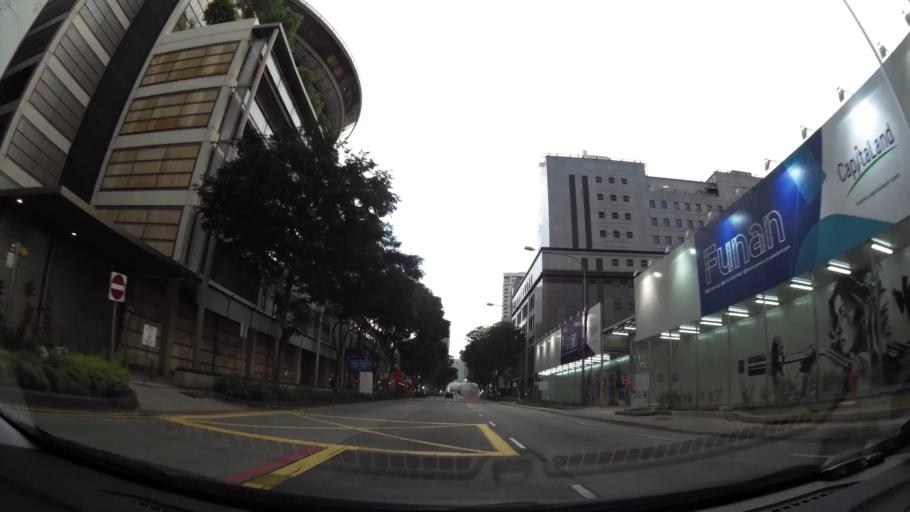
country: SG
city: Singapore
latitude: 1.2912
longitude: 103.8507
